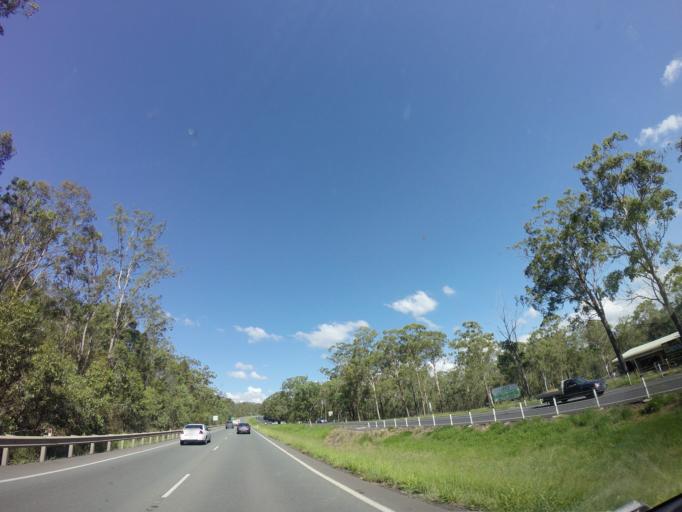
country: AU
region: Queensland
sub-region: Ipswich
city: Brassall
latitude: -27.5791
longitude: 152.7419
